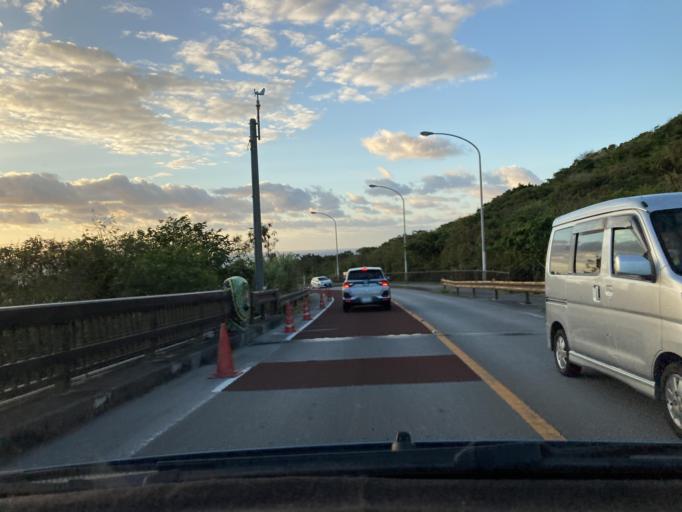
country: JP
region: Okinawa
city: Ginowan
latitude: 26.1655
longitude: 127.8161
